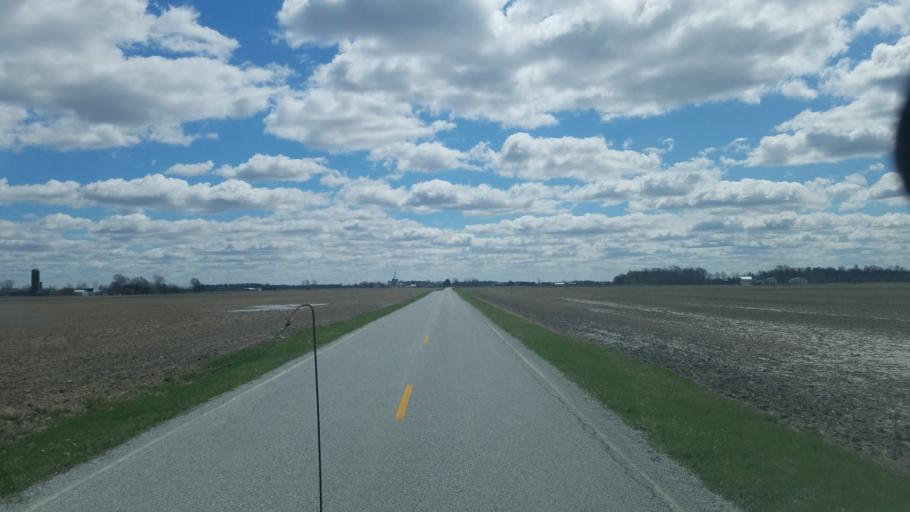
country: US
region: Ohio
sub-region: Hardin County
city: Kenton
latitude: 40.7307
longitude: -83.5741
